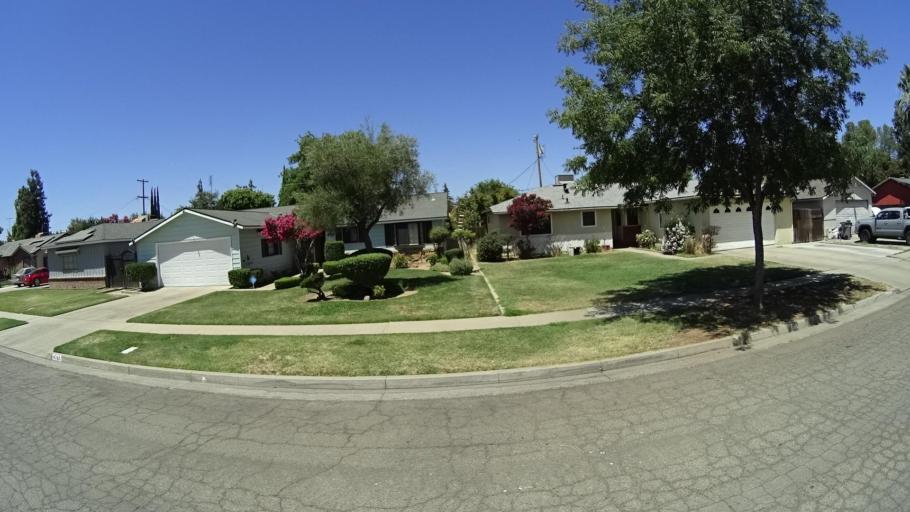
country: US
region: California
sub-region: Fresno County
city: Fresno
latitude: 36.8043
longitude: -119.7780
